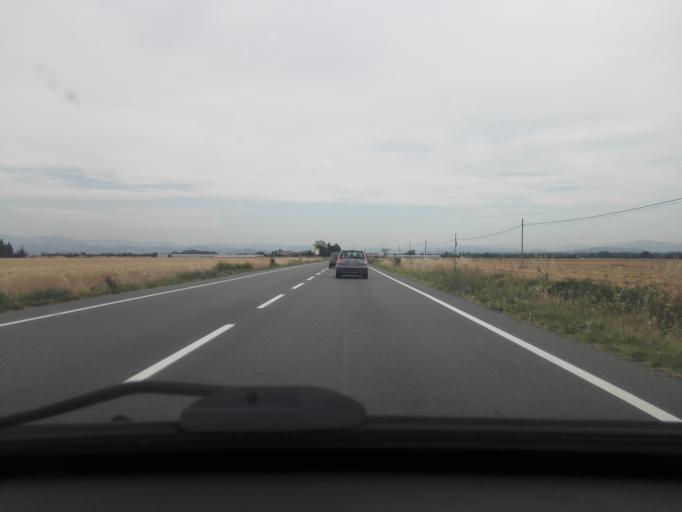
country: IT
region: Piedmont
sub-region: Provincia di Alessandria
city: Pozzolo Formigaro
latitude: 44.8170
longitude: 8.7570
